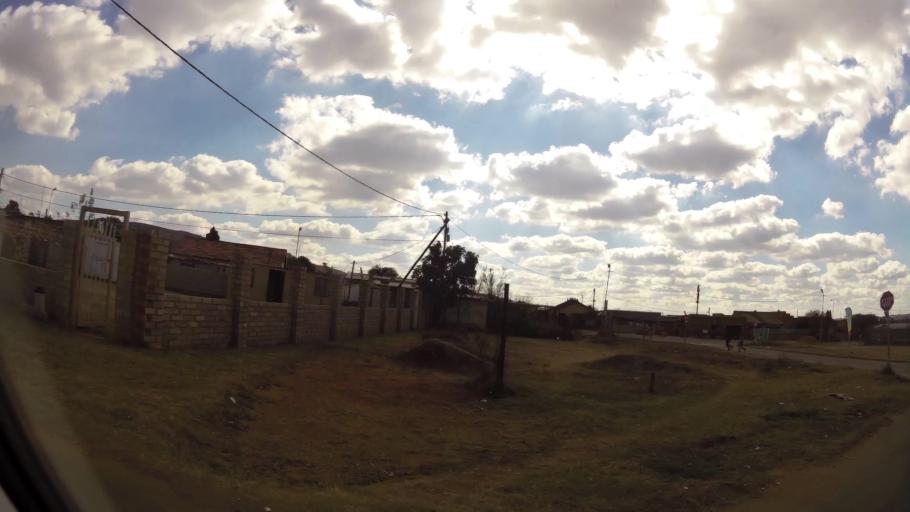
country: ZA
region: Gauteng
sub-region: City of Tshwane Metropolitan Municipality
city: Cullinan
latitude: -25.7051
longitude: 28.3972
